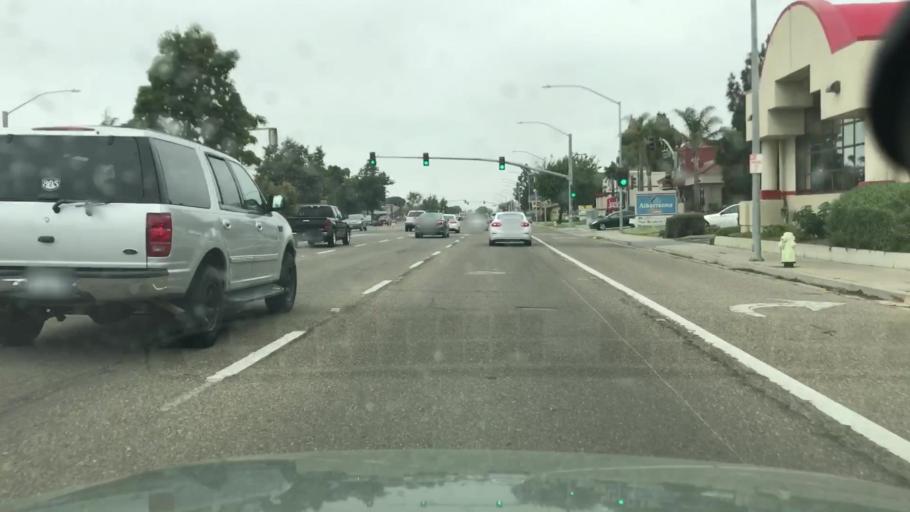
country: US
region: California
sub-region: Santa Barbara County
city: Santa Maria
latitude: 34.9175
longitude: -120.4358
